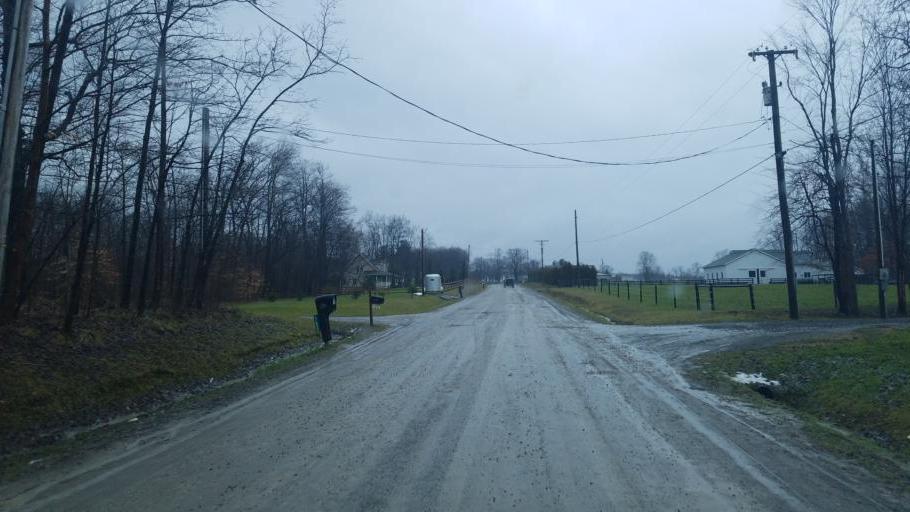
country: US
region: Ohio
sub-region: Geauga County
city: Middlefield
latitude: 41.4138
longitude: -81.0123
